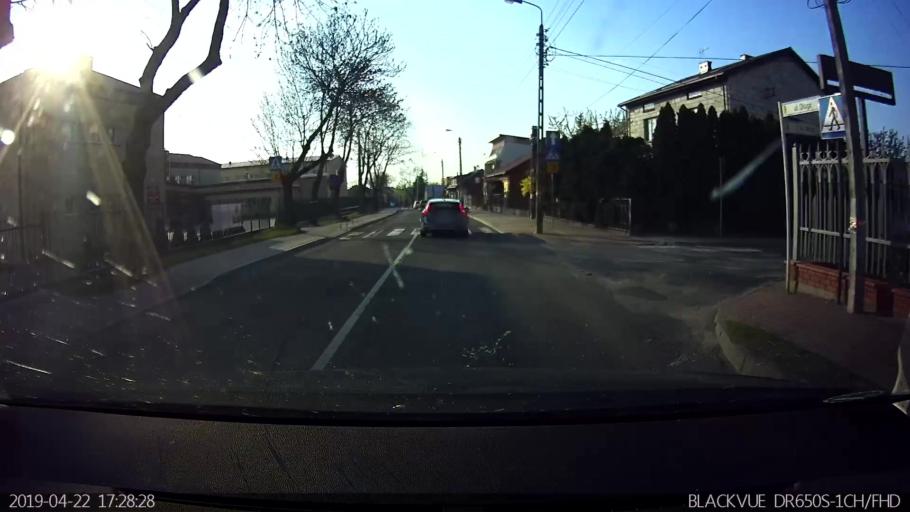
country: PL
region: Masovian Voivodeship
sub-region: Powiat sokolowski
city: Sokolow Podlaski
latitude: 52.4029
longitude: 22.2591
